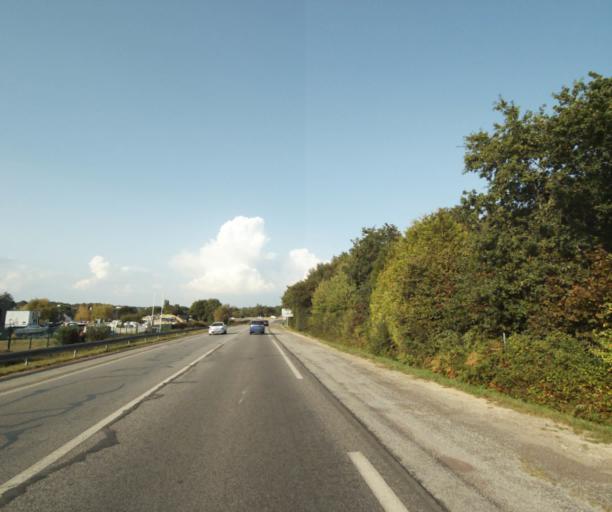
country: FR
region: Brittany
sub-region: Departement du Morbihan
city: Kervignac
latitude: 47.7575
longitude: -3.2851
